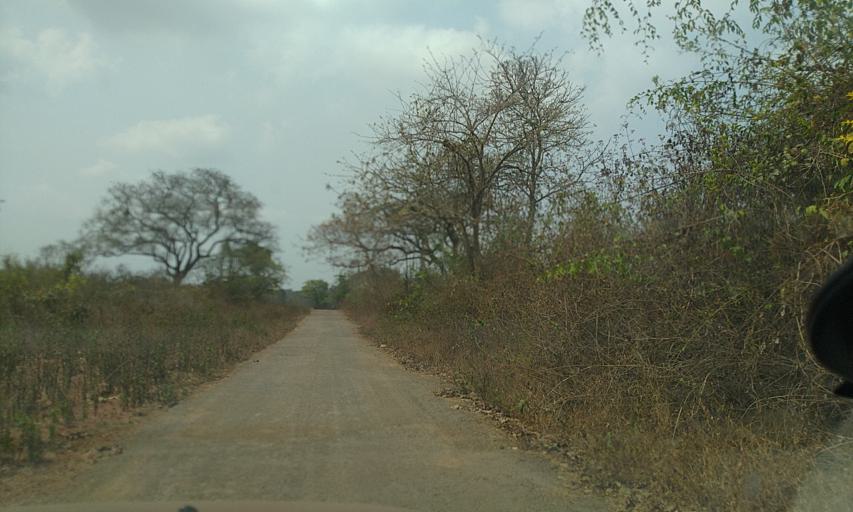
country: IN
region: Goa
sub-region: North Goa
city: Goa Velha
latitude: 15.4801
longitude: 73.9103
